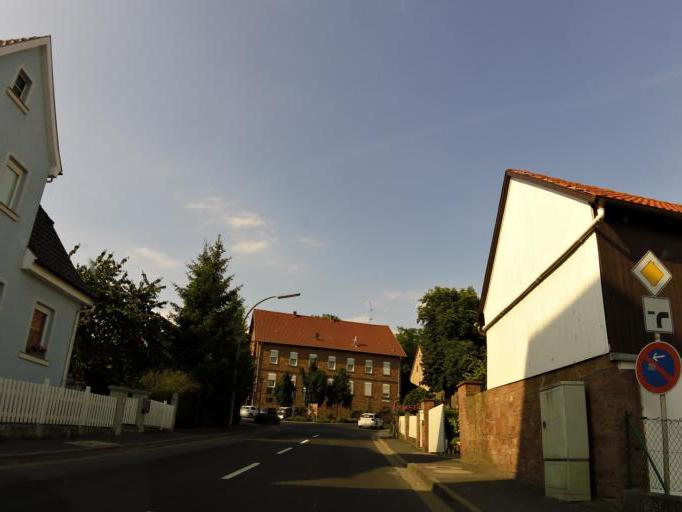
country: DE
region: Bavaria
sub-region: Regierungsbezirk Unterfranken
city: Marktheidenfeld
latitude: 49.8095
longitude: 9.6067
